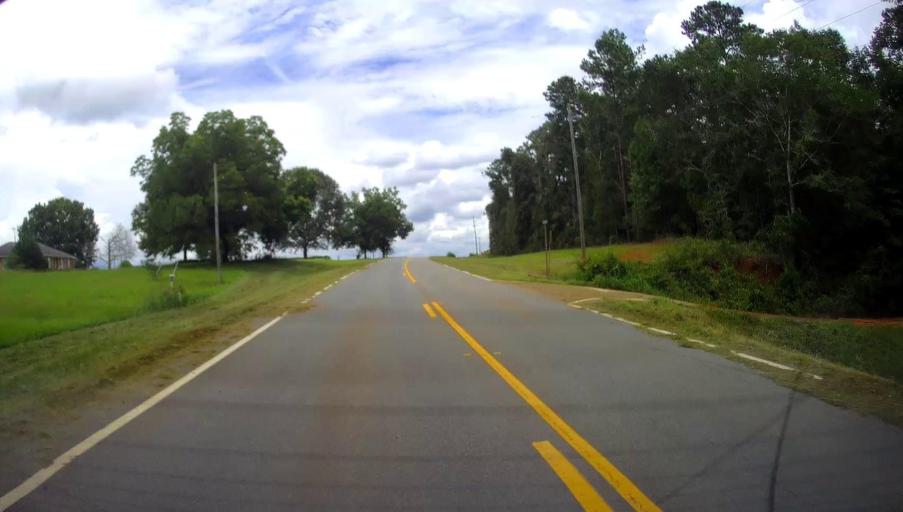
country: US
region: Georgia
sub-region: Macon County
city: Oglethorpe
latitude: 32.2719
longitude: -84.1833
